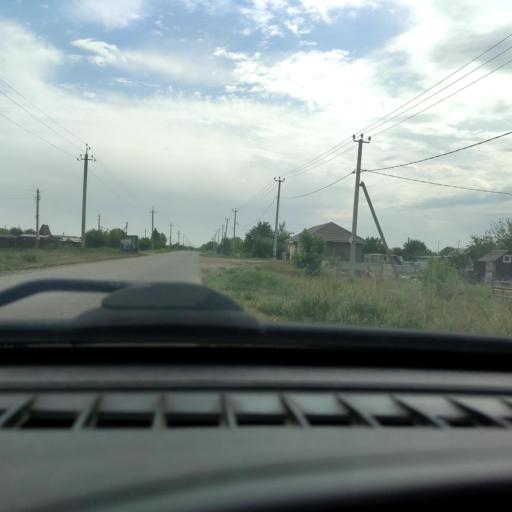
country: RU
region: Samara
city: Tol'yatti
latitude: 53.6438
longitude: 49.3260
